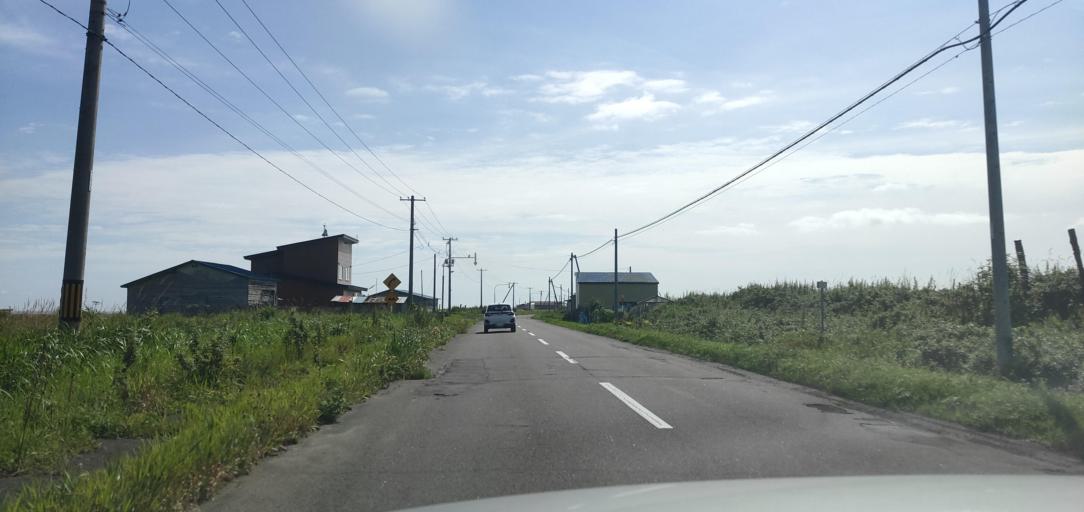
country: JP
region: Hokkaido
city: Shibetsu
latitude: 43.6376
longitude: 145.1672
